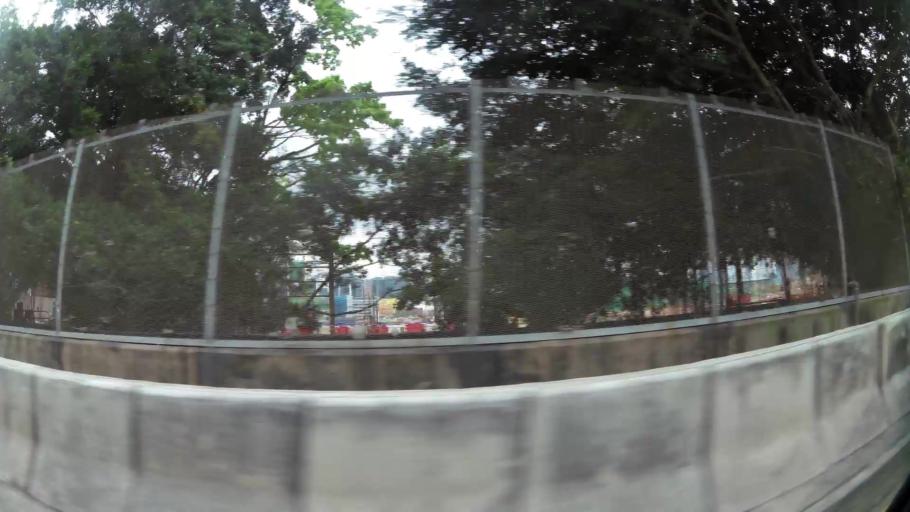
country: HK
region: Kowloon City
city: Kowloon
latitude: 22.3316
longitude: 114.1956
